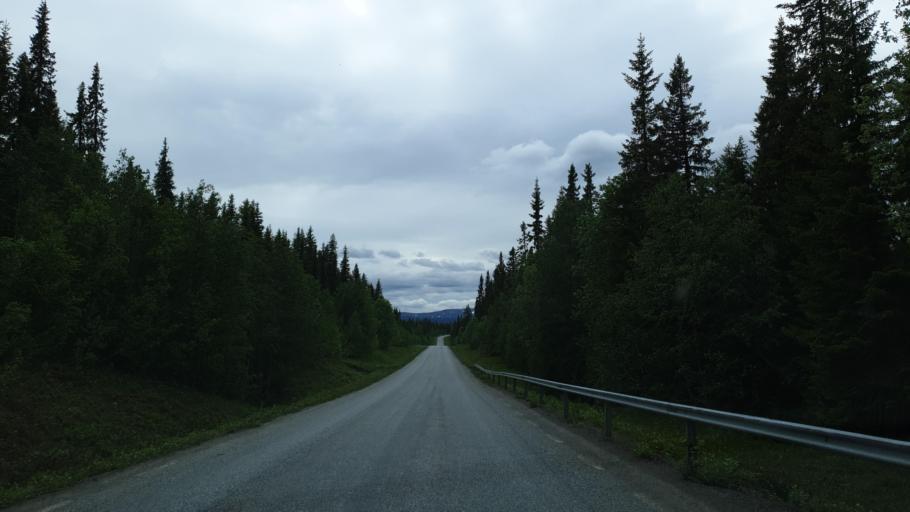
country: SE
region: Vaesterbotten
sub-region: Vilhelmina Kommun
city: Sjoberg
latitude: 65.4201
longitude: 16.1615
